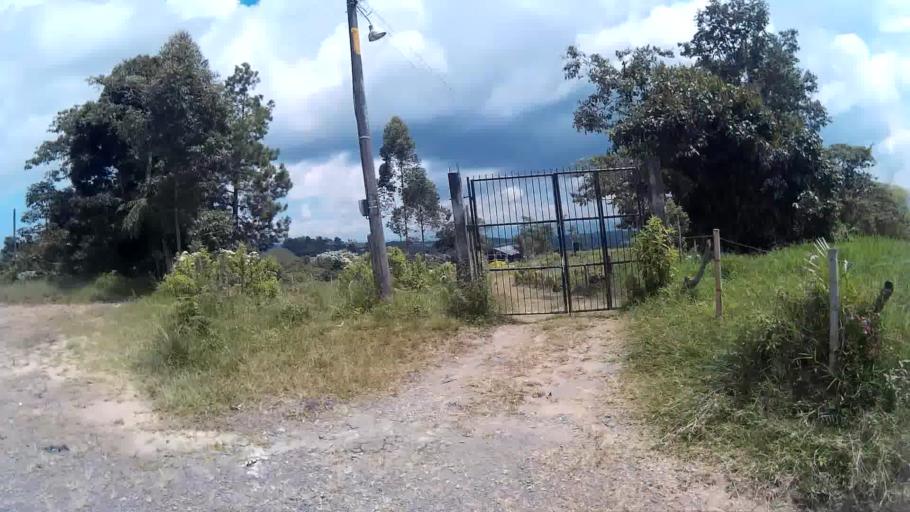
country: CO
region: Quindio
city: Filandia
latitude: 4.7134
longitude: -75.6532
